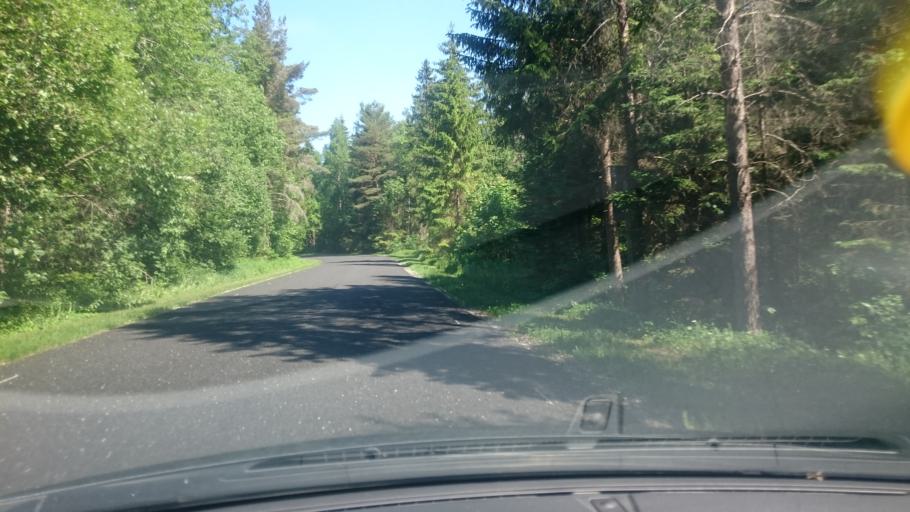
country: EE
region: Harju
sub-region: Rae vald
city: Vaida
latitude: 59.2095
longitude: 24.9494
